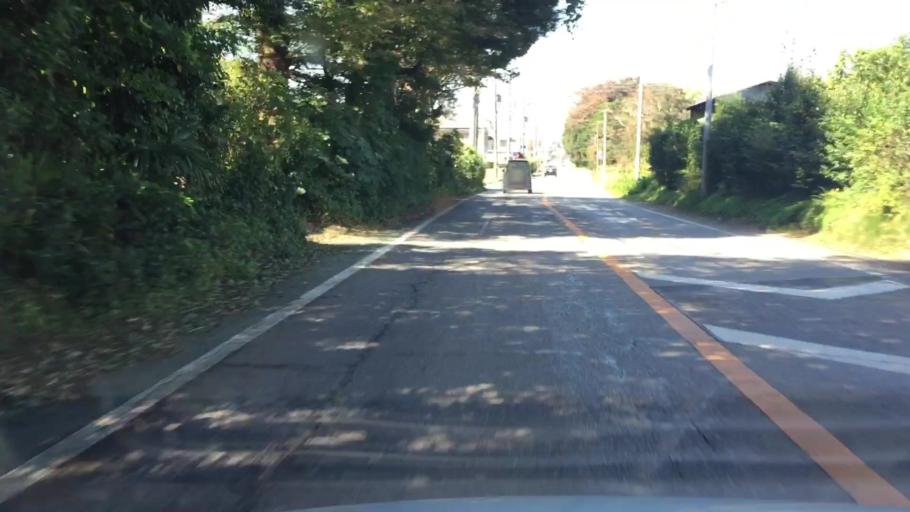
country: JP
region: Ibaraki
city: Fujishiro
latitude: 35.8578
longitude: 140.1311
